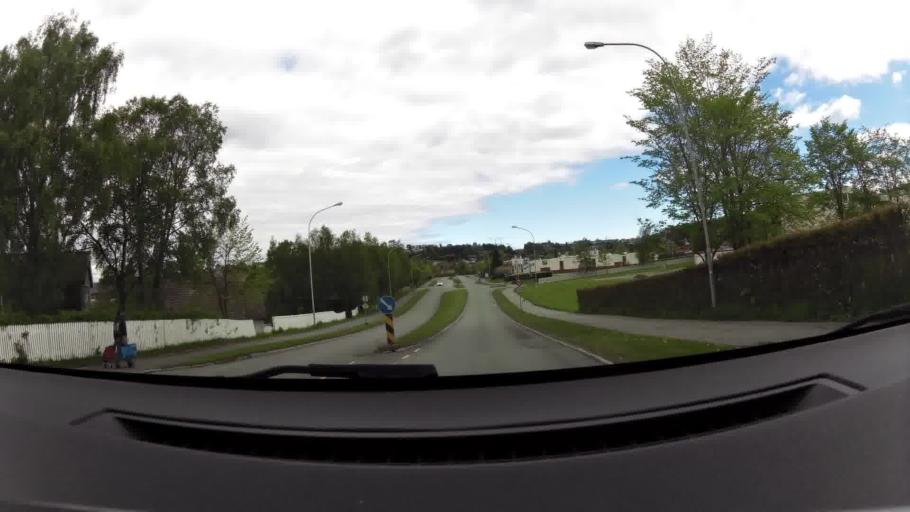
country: NO
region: Sor-Trondelag
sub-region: Trondheim
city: Trondheim
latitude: 63.4018
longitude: 10.4243
